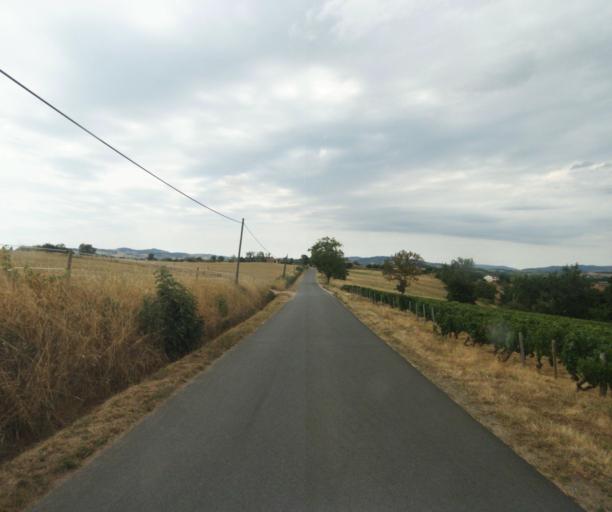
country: FR
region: Rhone-Alpes
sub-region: Departement du Rhone
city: Bully
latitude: 45.8825
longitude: 4.5539
